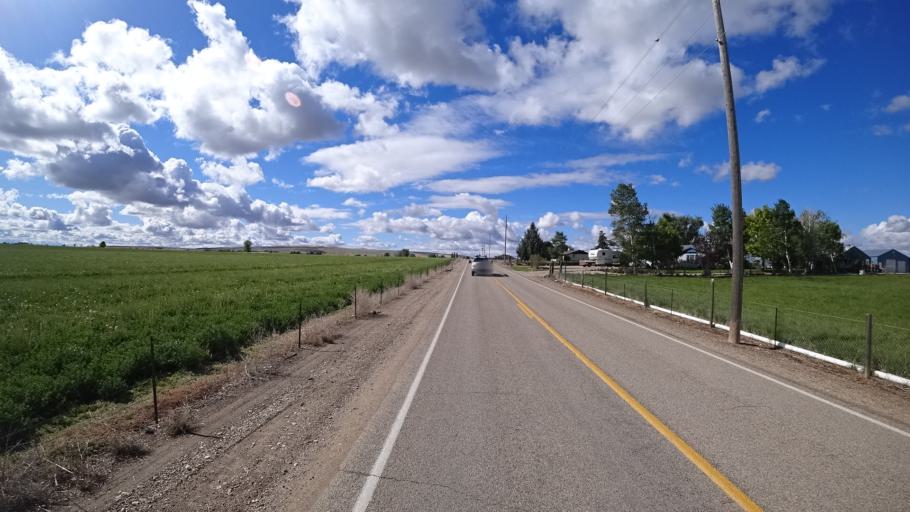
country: US
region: Idaho
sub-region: Ada County
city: Kuna
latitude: 43.4853
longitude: -116.4735
